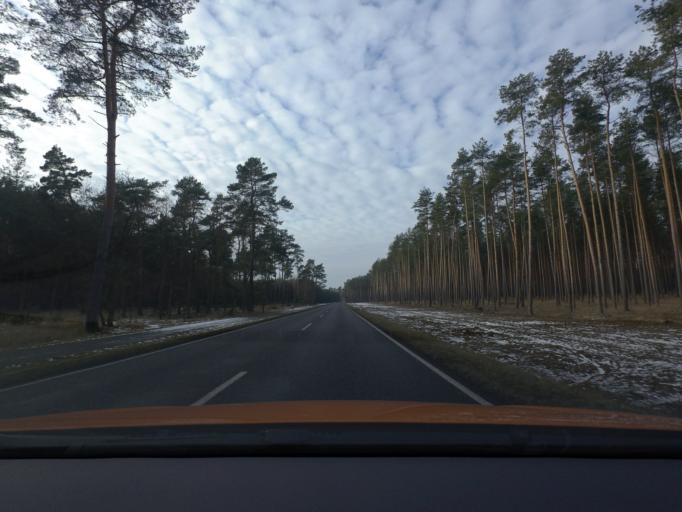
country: DE
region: Brandenburg
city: Ruthnick
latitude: 52.8994
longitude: 13.0783
